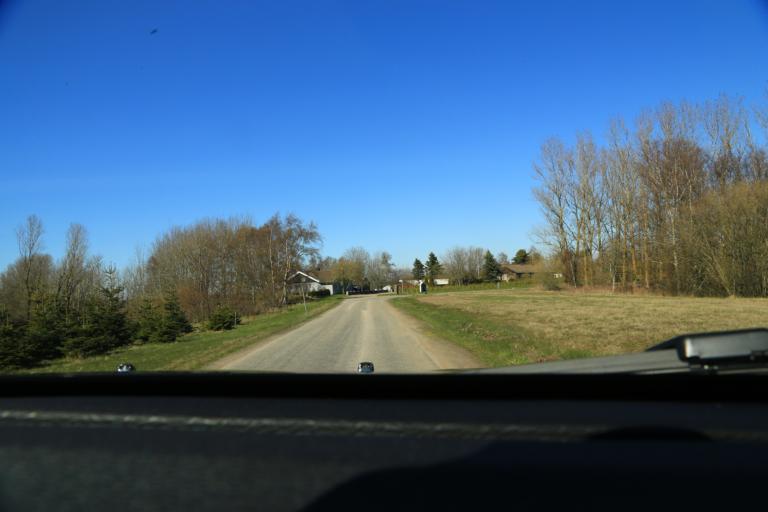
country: SE
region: Halland
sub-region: Varbergs Kommun
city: Traslovslage
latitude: 57.0795
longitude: 12.3065
